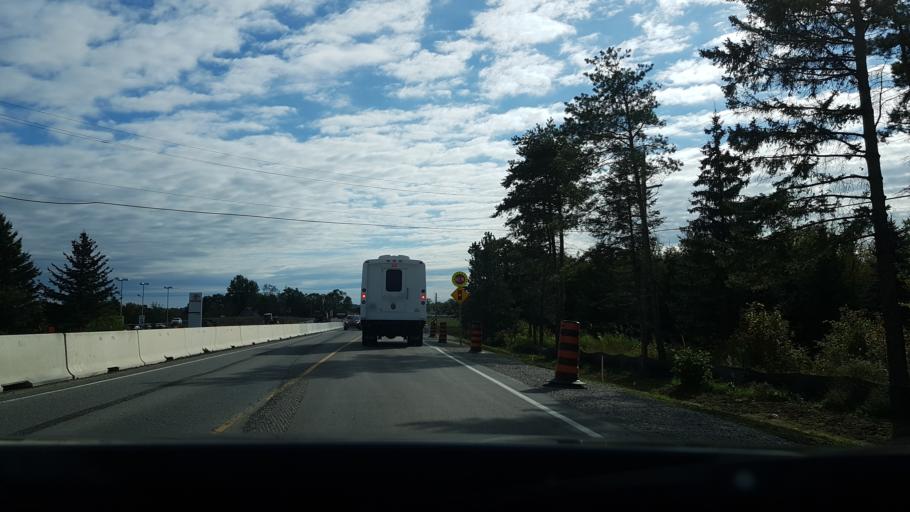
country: CA
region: Ontario
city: Orillia
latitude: 44.6127
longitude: -79.4679
